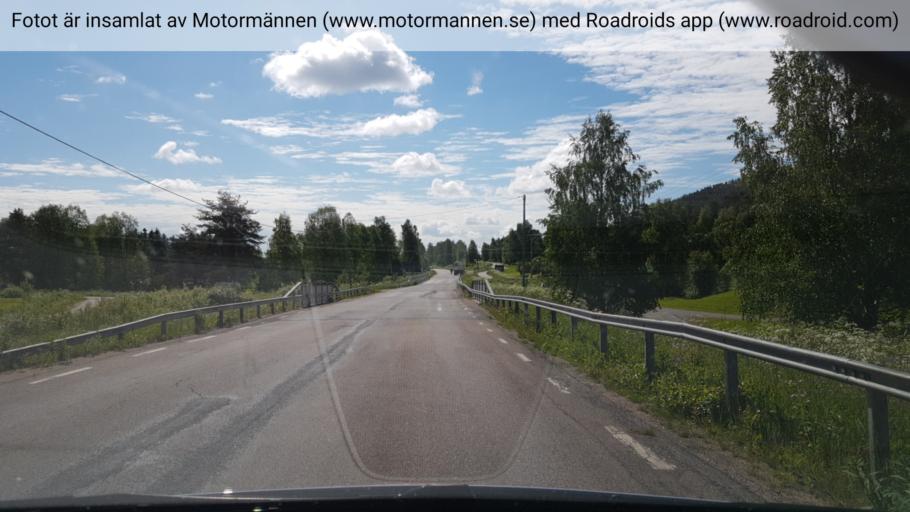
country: FI
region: Lapland
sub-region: Torniolaakso
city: Pello
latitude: 66.6589
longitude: 23.8515
